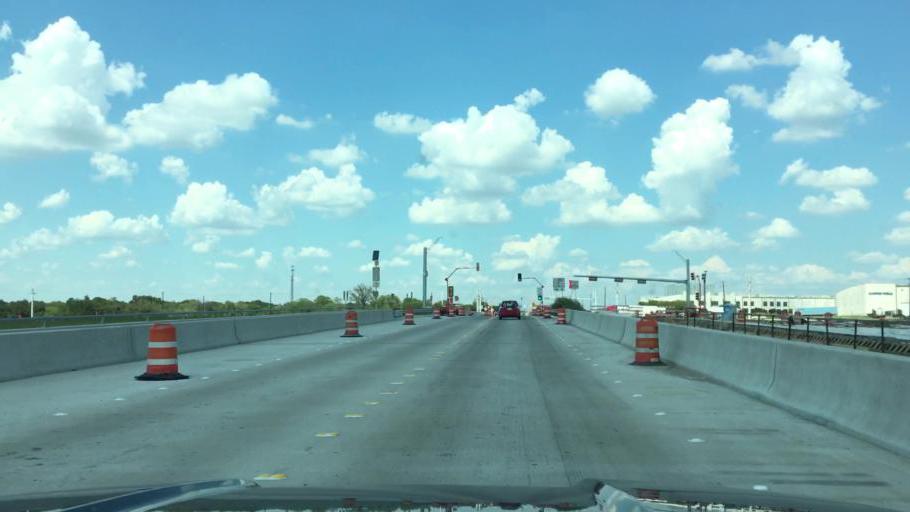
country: US
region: Texas
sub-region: Denton County
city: Justin
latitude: 33.0274
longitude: -97.3101
